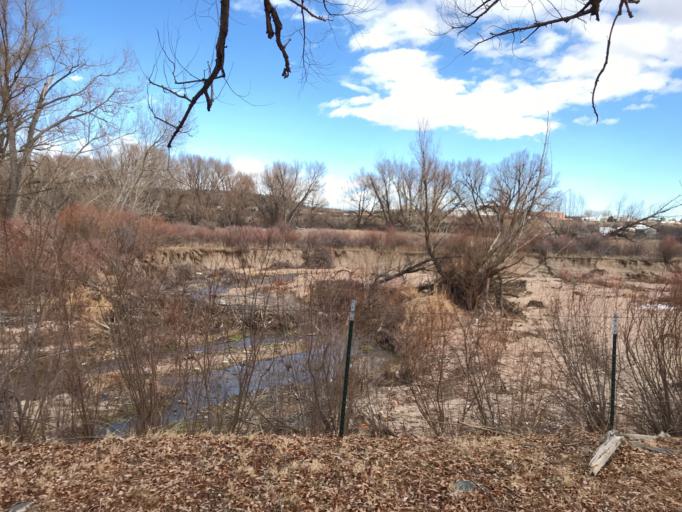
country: US
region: Colorado
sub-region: Douglas County
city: Castle Rock
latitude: 39.4006
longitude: -104.8743
